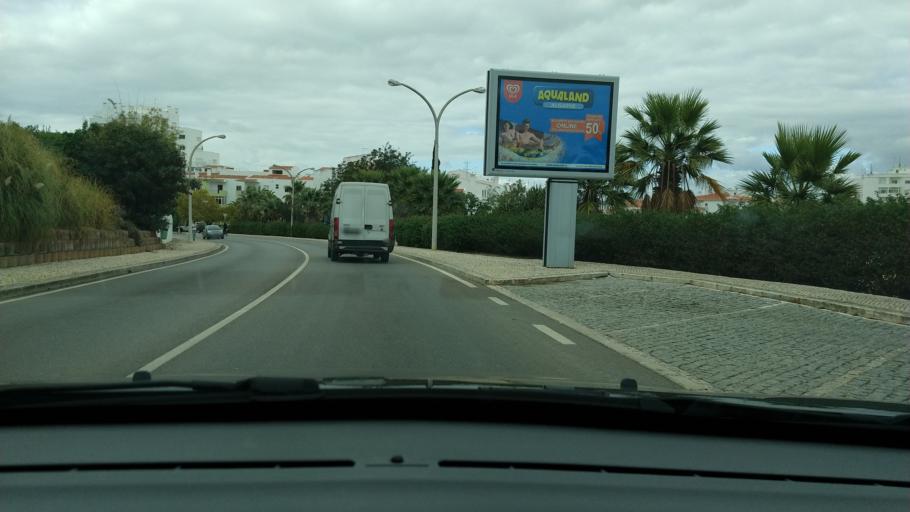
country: PT
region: Faro
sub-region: Lagos
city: Lagos
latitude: 37.0992
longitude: -8.6796
